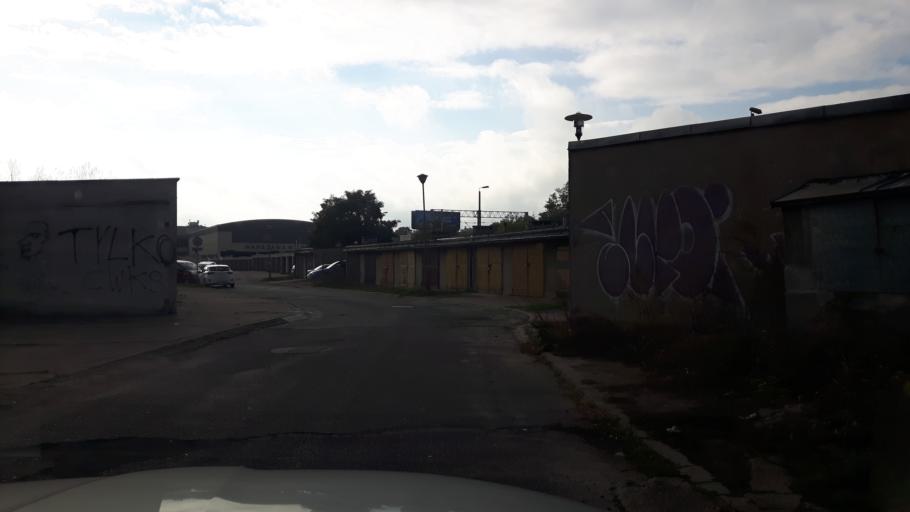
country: PL
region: Masovian Voivodeship
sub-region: Warszawa
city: Praga Polnoc
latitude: 52.2571
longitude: 21.0433
